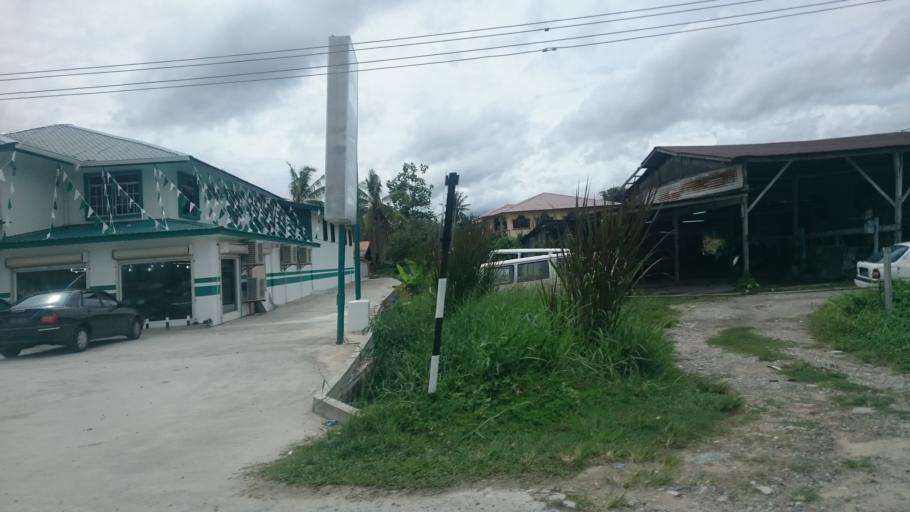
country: BN
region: Brunei and Muara
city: Bandar Seri Begawan
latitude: 4.8357
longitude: 114.8446
